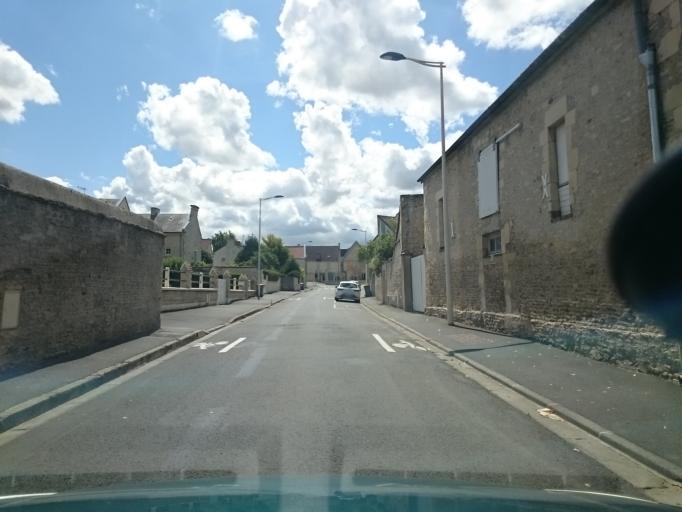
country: FR
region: Lower Normandy
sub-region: Departement du Calvados
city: Ifs
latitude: 49.1391
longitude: -0.3491
